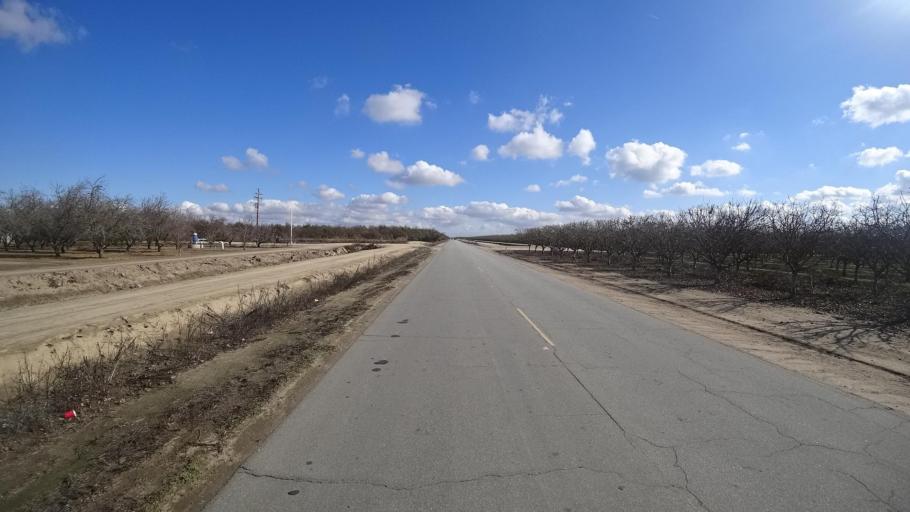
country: US
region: California
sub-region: Kern County
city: McFarland
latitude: 35.6742
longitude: -119.3128
